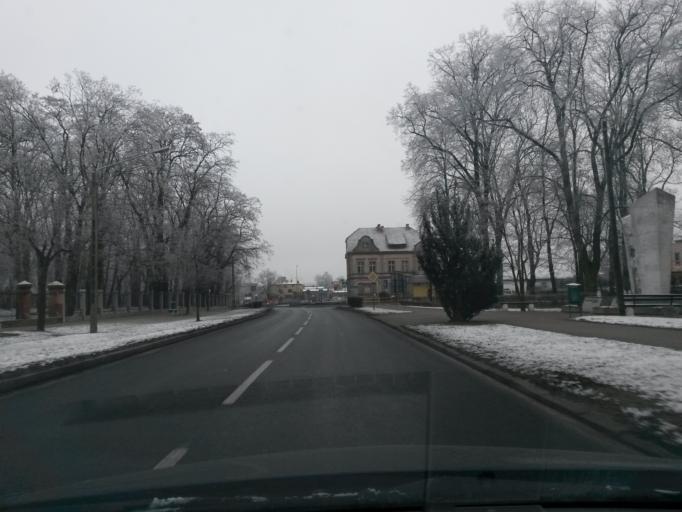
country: PL
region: Kujawsko-Pomorskie
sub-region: Powiat mogilenski
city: Strzelno
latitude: 52.6274
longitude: 18.1675
